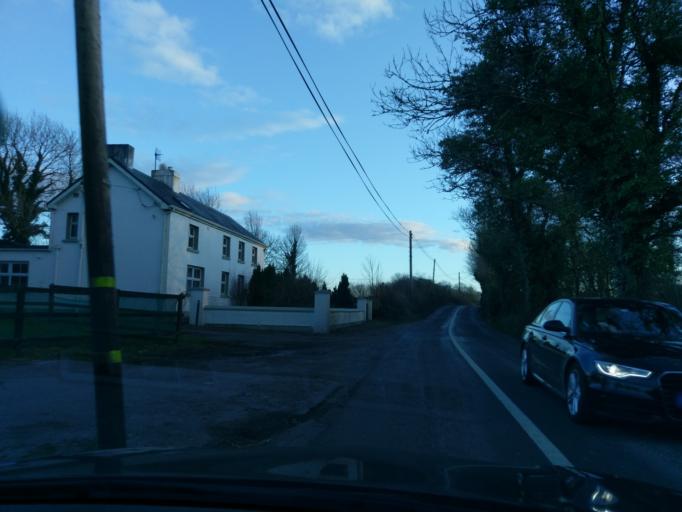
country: IE
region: Connaught
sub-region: County Galway
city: Athenry
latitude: 53.3148
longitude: -8.6176
